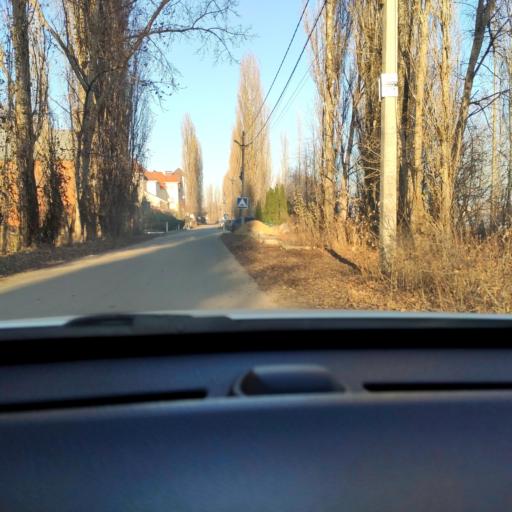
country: RU
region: Voronezj
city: Voronezh
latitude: 51.6978
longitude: 39.2351
